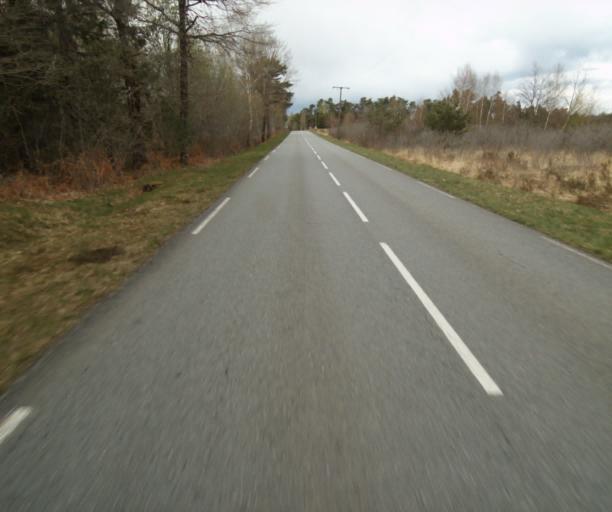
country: FR
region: Limousin
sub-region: Departement de la Correze
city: Saint-Privat
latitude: 45.2082
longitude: 2.0042
